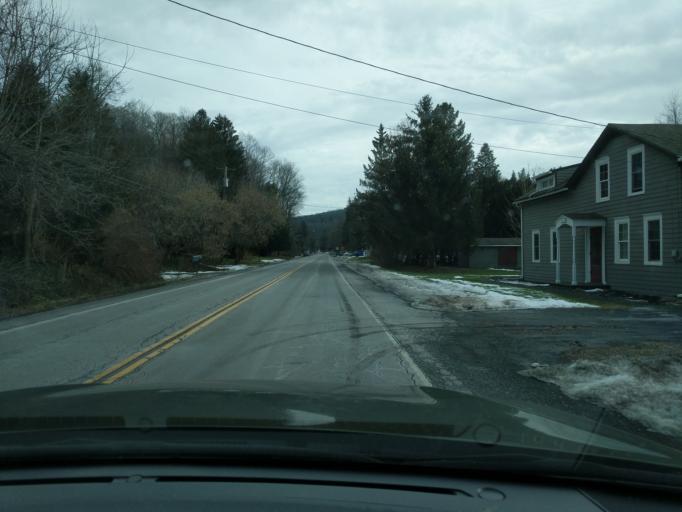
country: US
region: New York
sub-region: Tompkins County
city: East Ithaca
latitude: 42.3828
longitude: -76.4003
